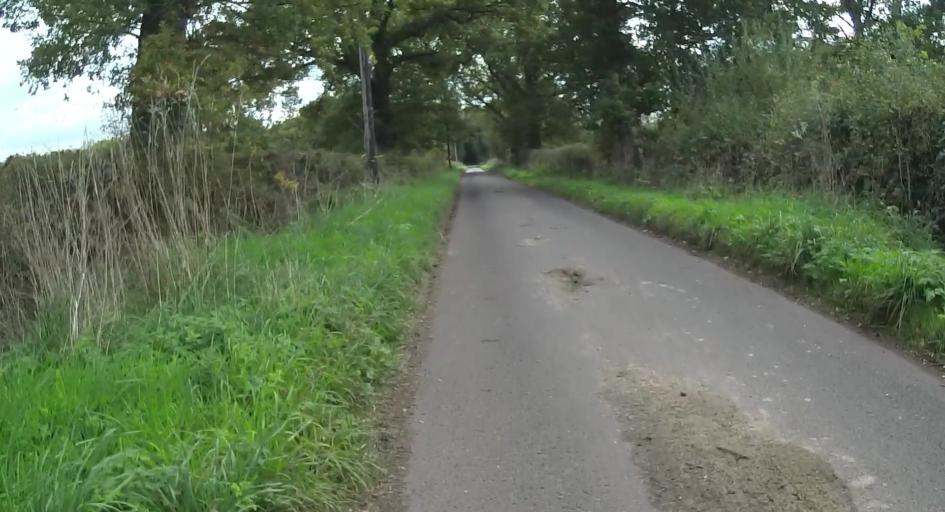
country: GB
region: England
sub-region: Hampshire
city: Eversley
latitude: 51.3628
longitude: -0.9059
